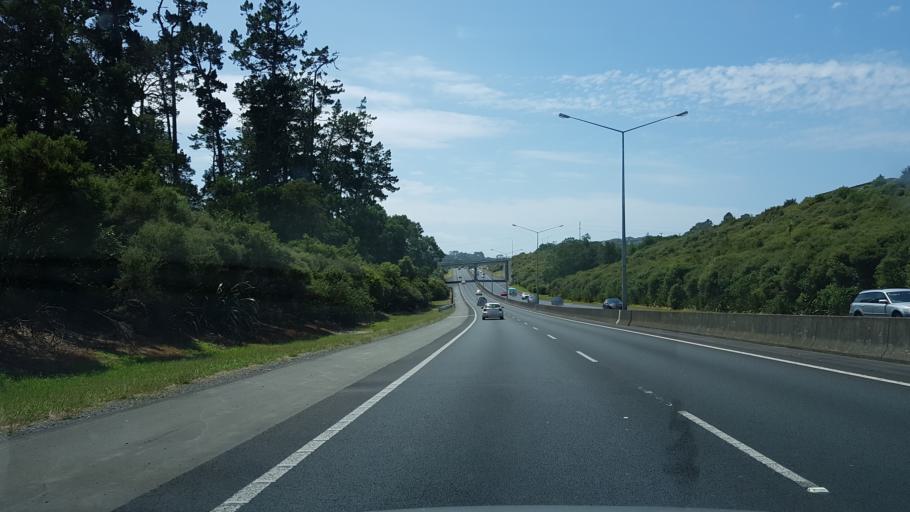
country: NZ
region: Auckland
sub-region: Auckland
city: North Shore
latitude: -36.7749
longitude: 174.6840
